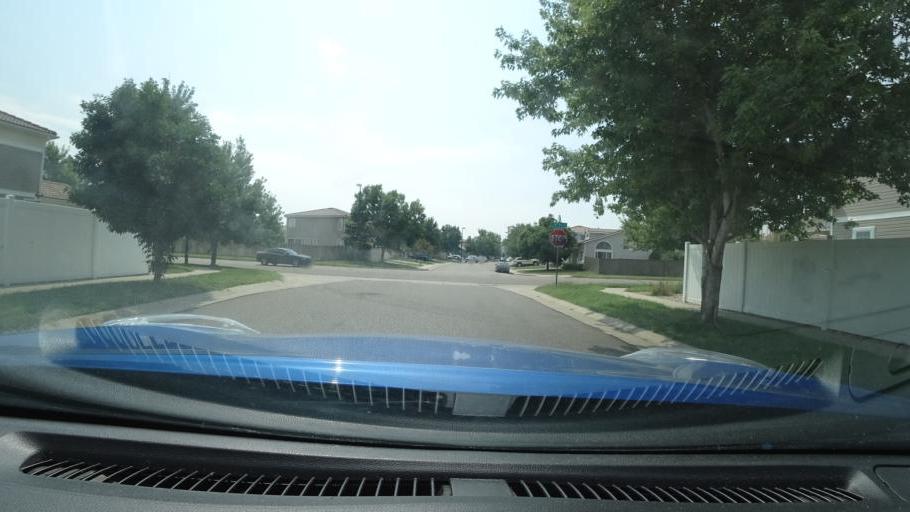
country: US
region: Colorado
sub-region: Adams County
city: Aurora
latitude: 39.7818
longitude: -104.7585
